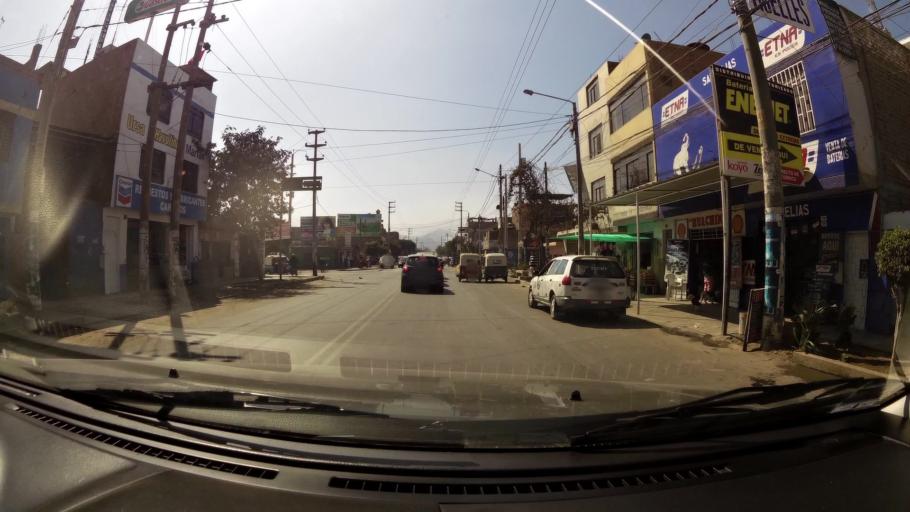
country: PE
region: Ica
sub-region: Provincia de Ica
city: Ica
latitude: -14.0615
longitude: -75.7220
